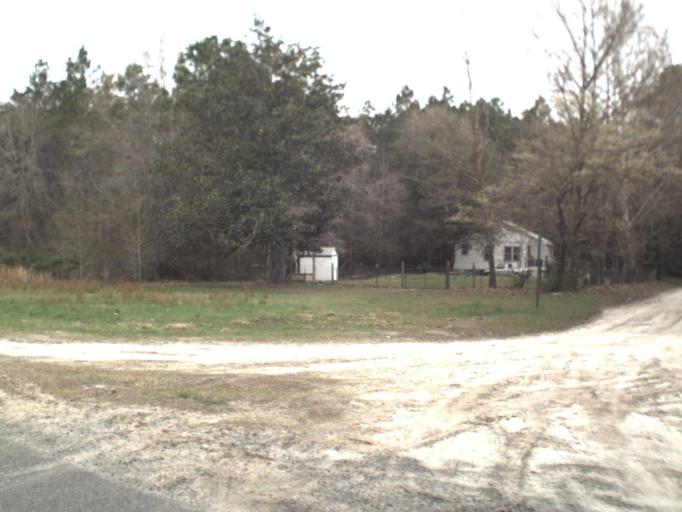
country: US
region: Florida
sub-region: Jefferson County
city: Monticello
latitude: 30.4987
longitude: -83.7464
